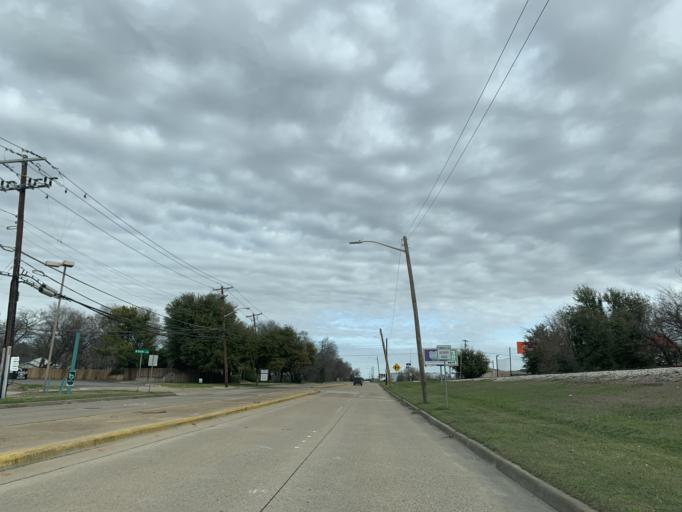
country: US
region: Texas
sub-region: Tarrant County
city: Edgecliff Village
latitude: 32.6950
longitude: -97.3599
